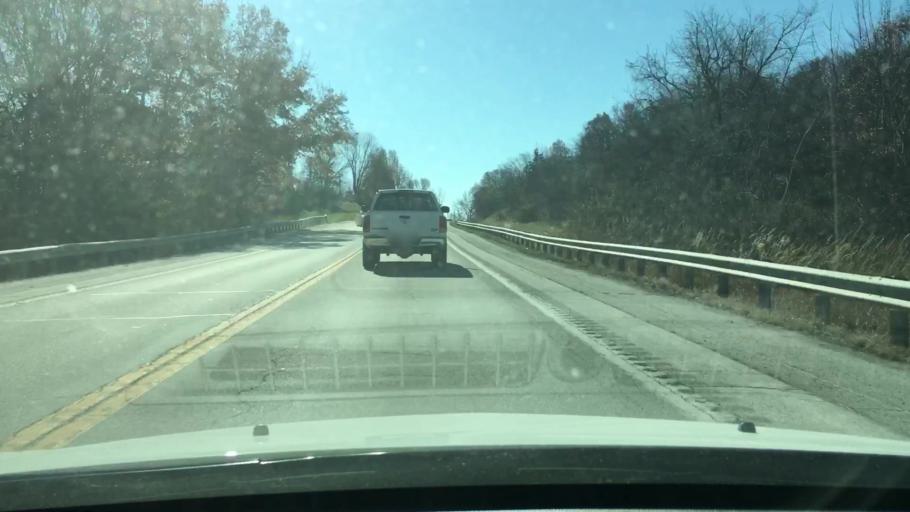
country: US
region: Missouri
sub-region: Pike County
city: Louisiana
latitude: 39.4349
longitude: -91.0800
